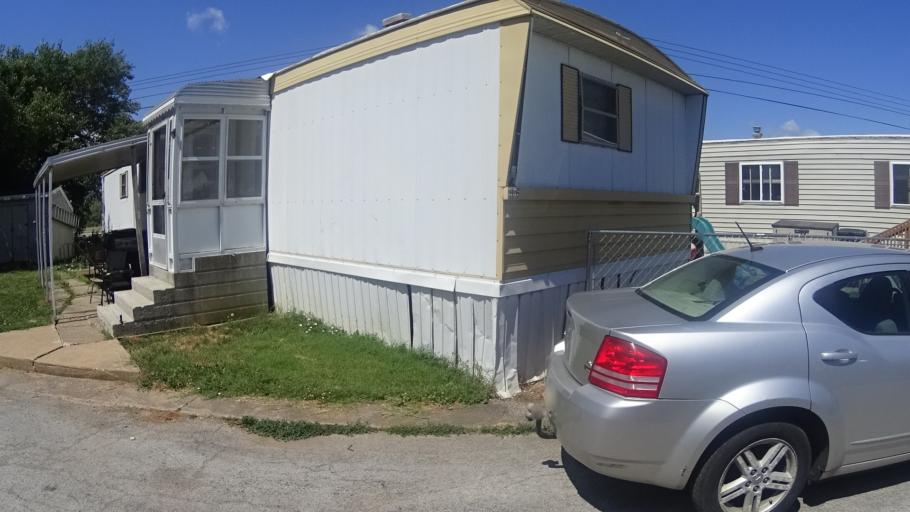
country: US
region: Ohio
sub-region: Erie County
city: Sandusky
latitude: 41.4315
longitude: -82.7085
